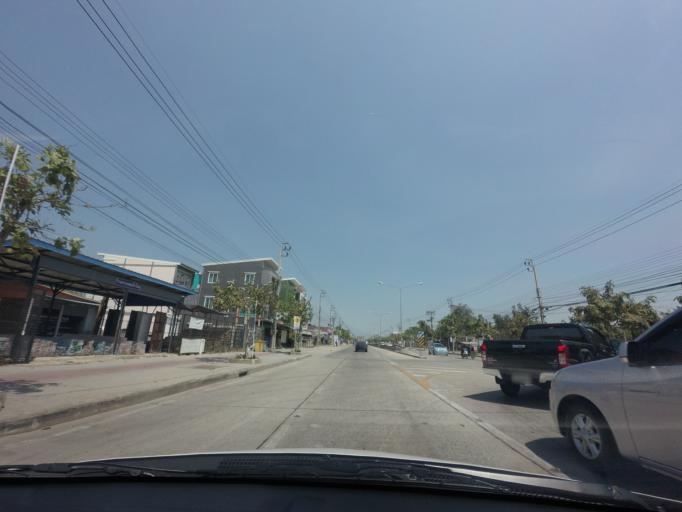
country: TH
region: Bangkok
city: Nong Chok
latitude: 13.8540
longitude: 100.8308
